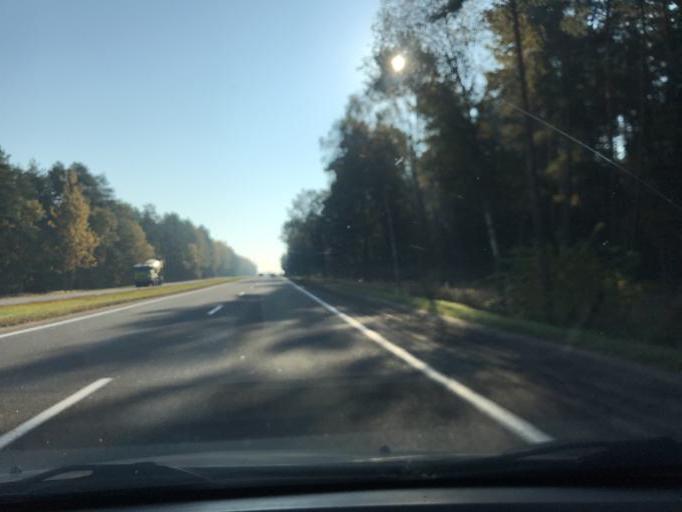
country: BY
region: Minsk
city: Dukora
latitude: 53.6251
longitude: 28.0363
